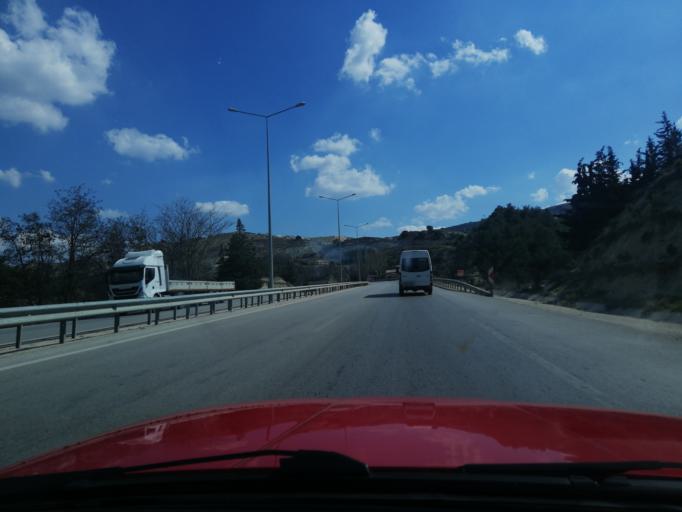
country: TR
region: Burdur
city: Burdur
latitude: 37.7042
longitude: 30.3066
